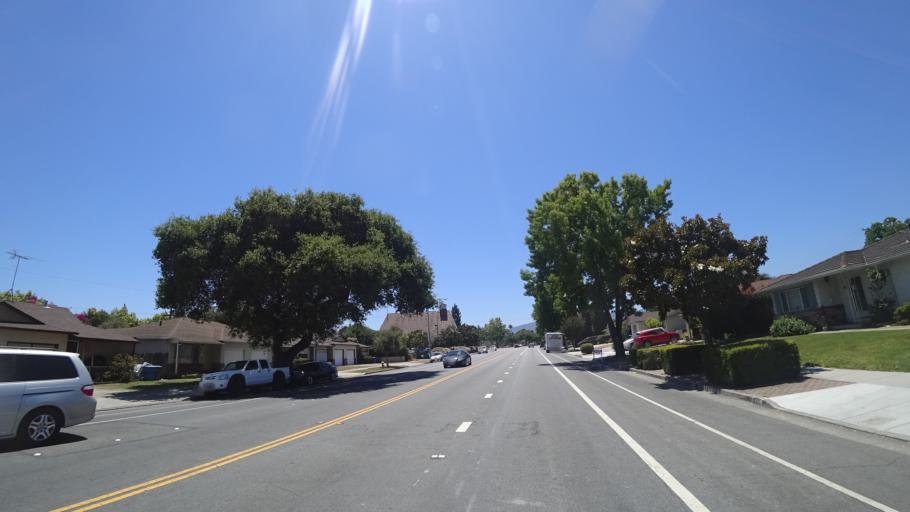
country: US
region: California
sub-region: Santa Clara County
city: Cupertino
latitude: 37.3121
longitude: -122.0135
